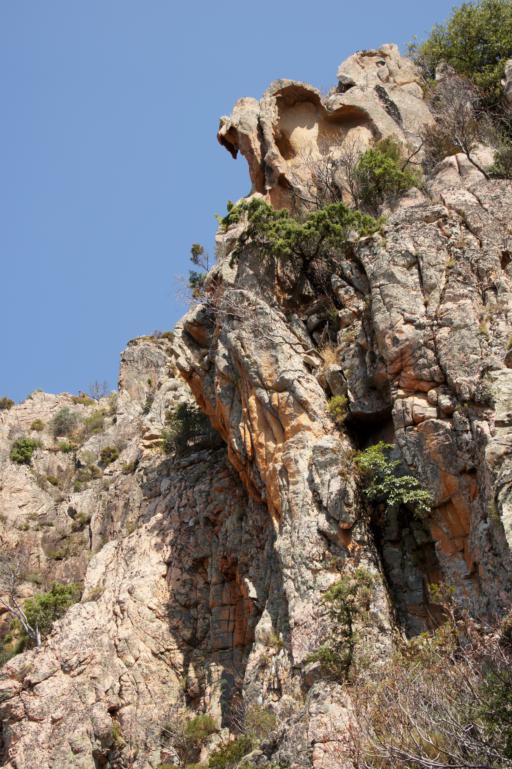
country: FR
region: Corsica
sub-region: Departement de la Corse-du-Sud
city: Cargese
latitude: 42.2444
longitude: 8.6537
